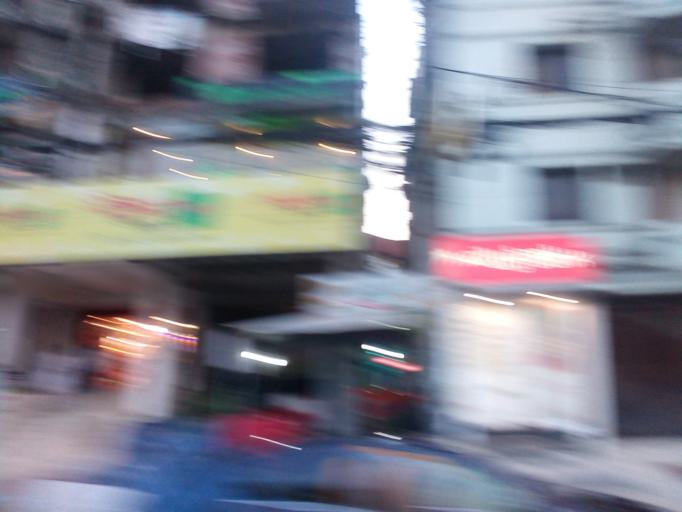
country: BD
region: Dhaka
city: Tungi
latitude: 23.8790
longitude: 90.3907
